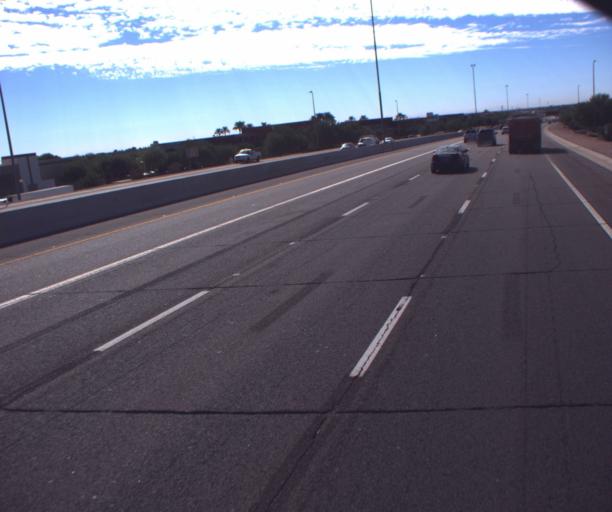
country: US
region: Arizona
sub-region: Maricopa County
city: Paradise Valley
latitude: 33.6275
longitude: -111.8906
